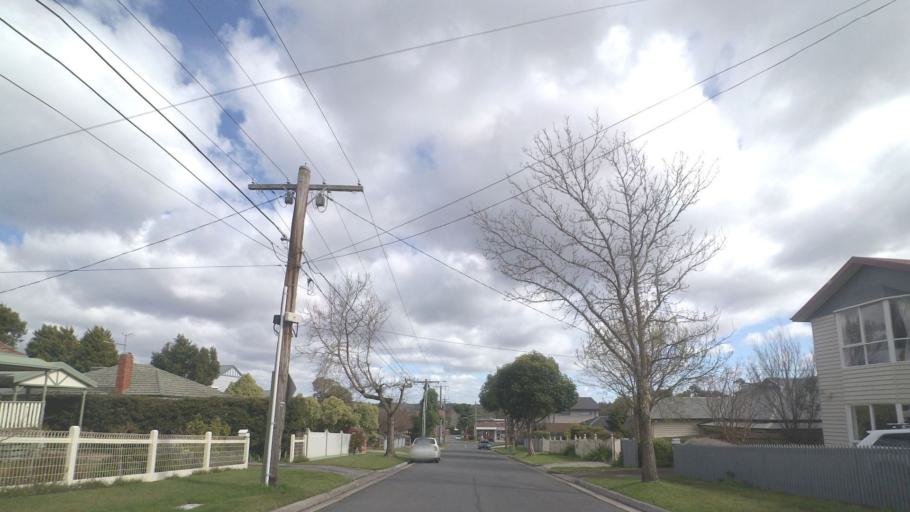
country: AU
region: Victoria
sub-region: Maroondah
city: Heathmont
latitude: -37.8288
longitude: 145.2386
